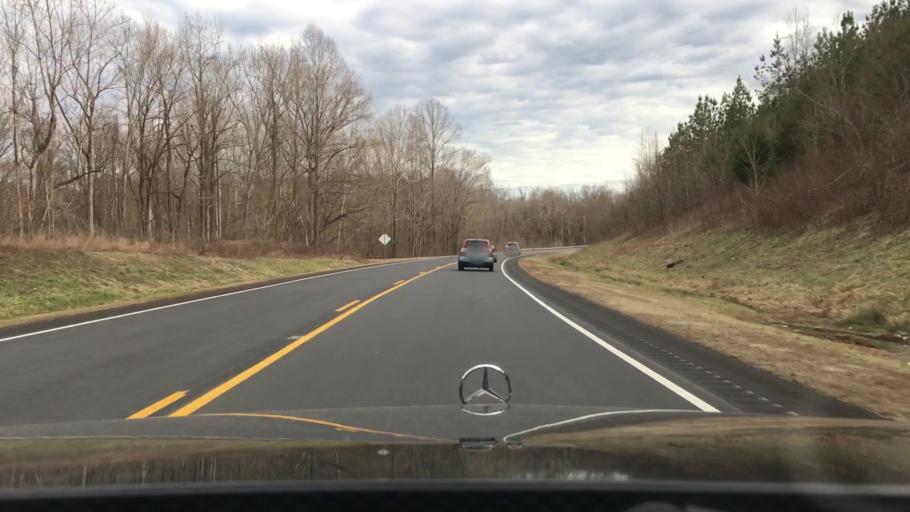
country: US
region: North Carolina
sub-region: Caswell County
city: Yanceyville
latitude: 36.3180
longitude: -79.2233
